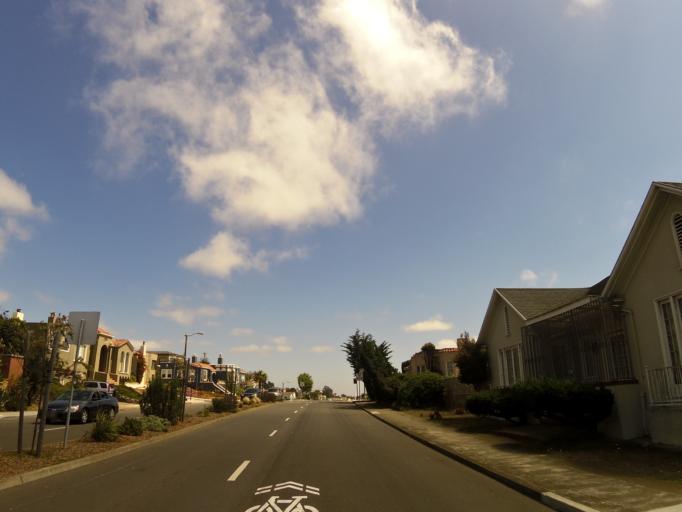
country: US
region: California
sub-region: San Mateo County
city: Daly City
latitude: 37.7312
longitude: -122.4566
